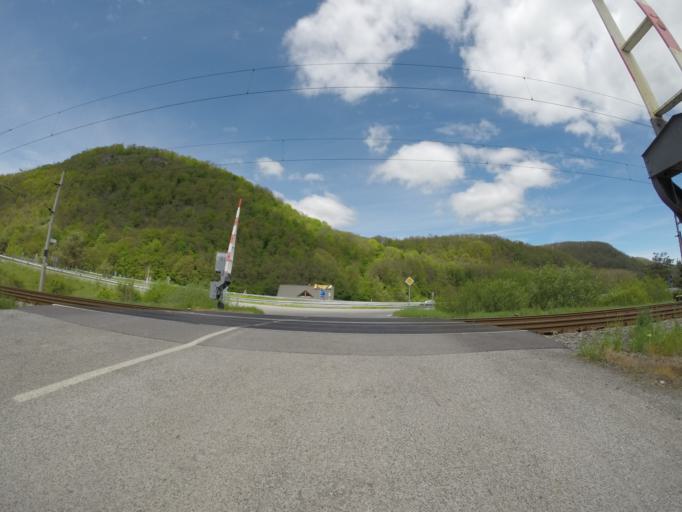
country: SK
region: Banskobystricky
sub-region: Okres Banska Bystrica
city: Zvolen
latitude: 48.5652
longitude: 19.0436
